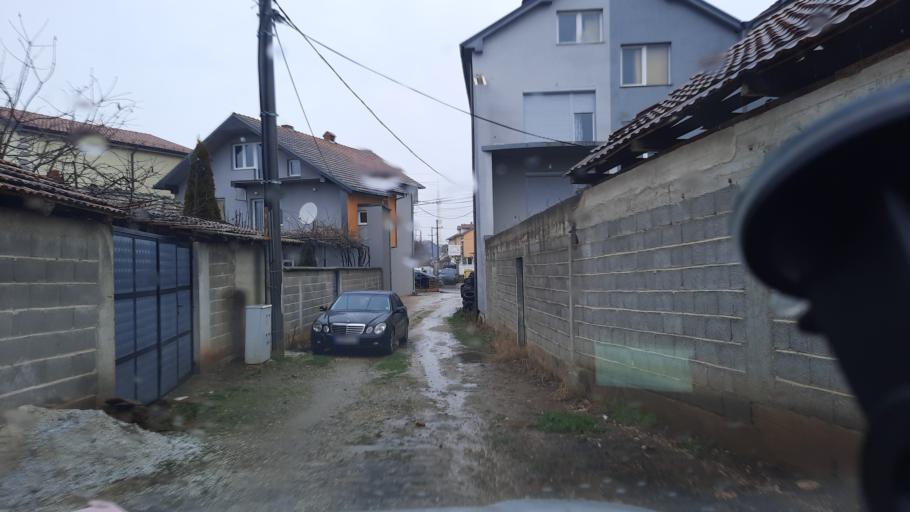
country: MK
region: Opstina Lipkovo
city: Matejche
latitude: 42.1233
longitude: 21.5980
